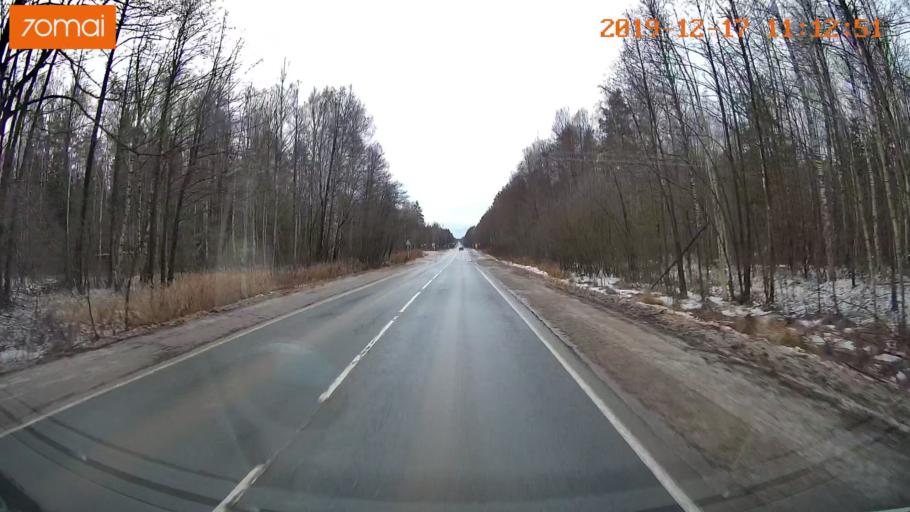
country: RU
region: Vladimir
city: Gus'-Khrustal'nyy
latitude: 55.5707
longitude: 40.6245
